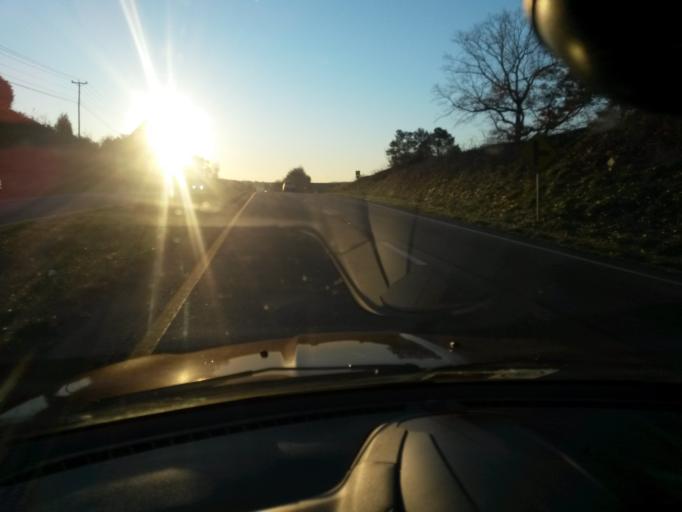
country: US
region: Virginia
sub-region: Franklin County
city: Rocky Mount
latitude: 37.0850
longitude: -79.9282
